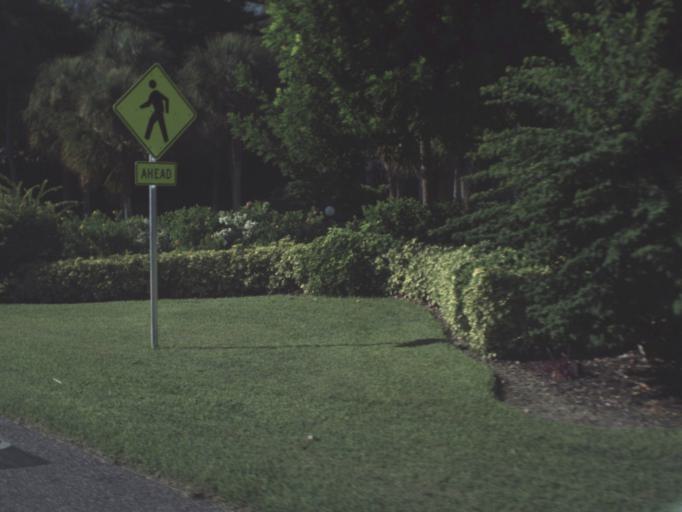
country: US
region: Florida
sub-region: Manatee County
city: Longboat Key
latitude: 27.4104
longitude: -82.6571
